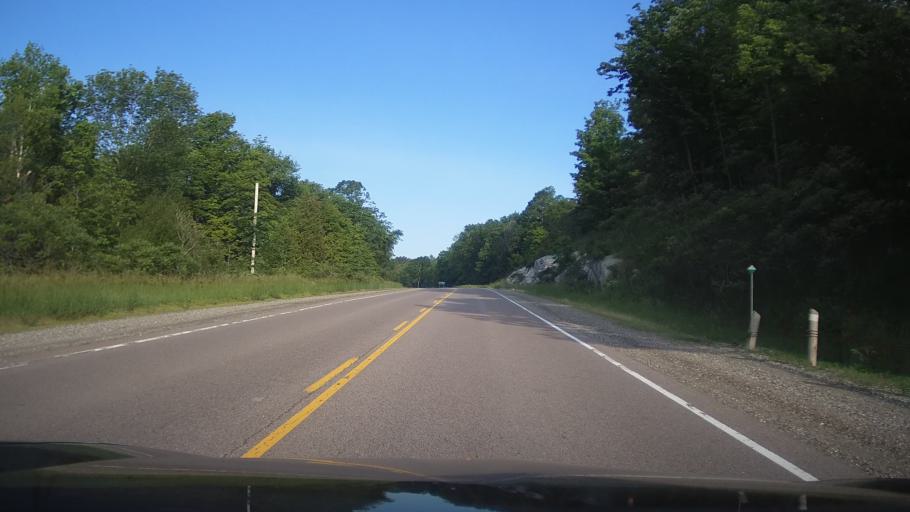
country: CA
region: Ontario
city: Skatepark
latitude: 44.7581
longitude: -76.7938
